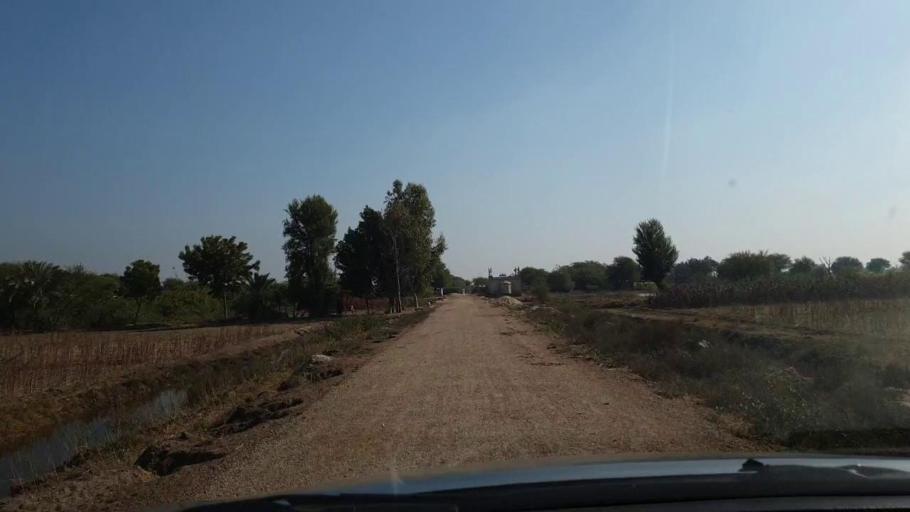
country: PK
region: Sindh
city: Jhol
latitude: 25.8670
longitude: 68.8955
